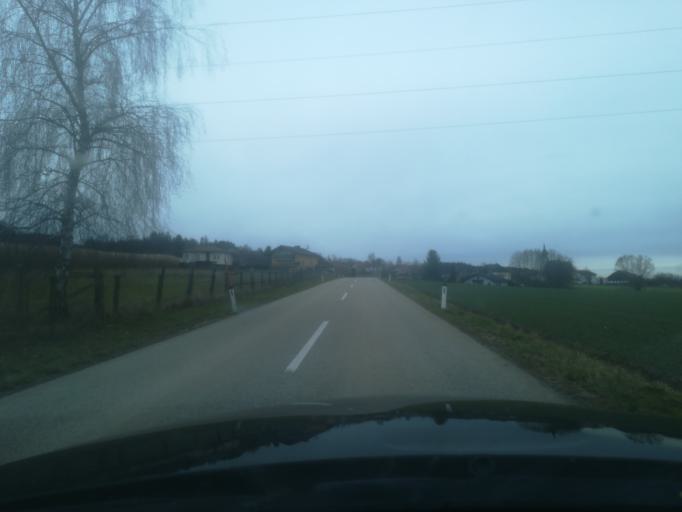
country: AT
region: Upper Austria
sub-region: Wels-Land
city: Neukirchen bei Lambach
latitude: 48.0968
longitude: 13.8199
